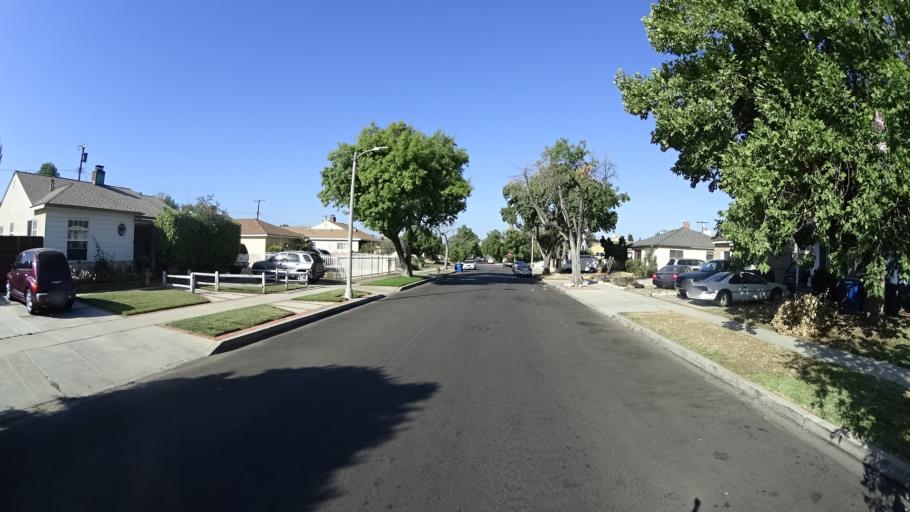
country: US
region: California
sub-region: Los Angeles County
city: Van Nuys
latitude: 34.2289
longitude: -118.4279
